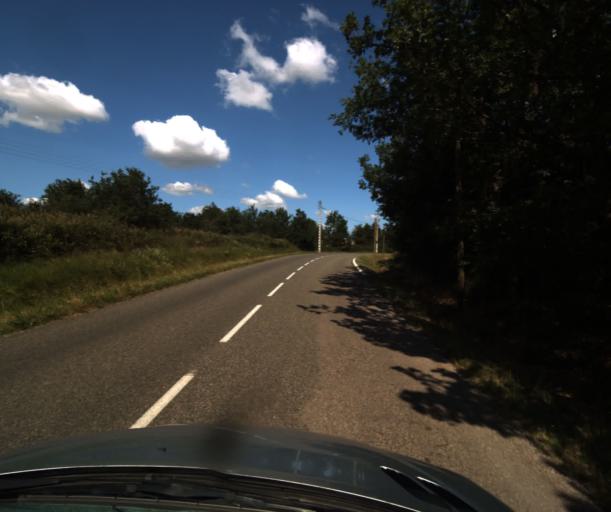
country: FR
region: Midi-Pyrenees
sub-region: Departement du Tarn-et-Garonne
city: Campsas
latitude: 43.9042
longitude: 1.2935
